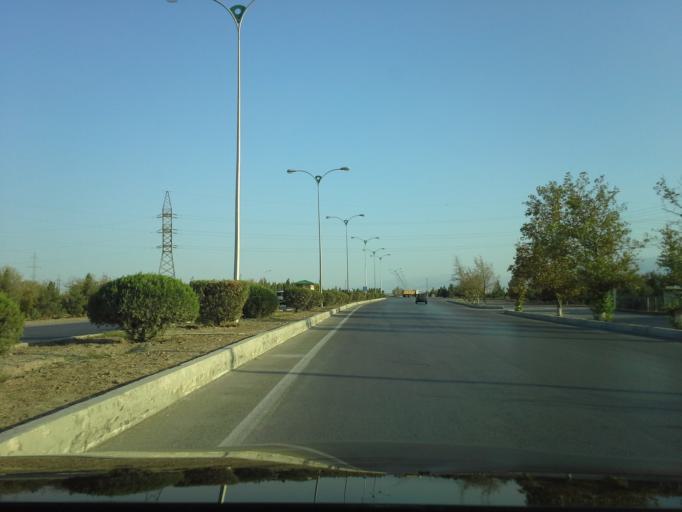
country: TM
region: Ahal
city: Abadan
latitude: 38.0253
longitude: 58.1995
